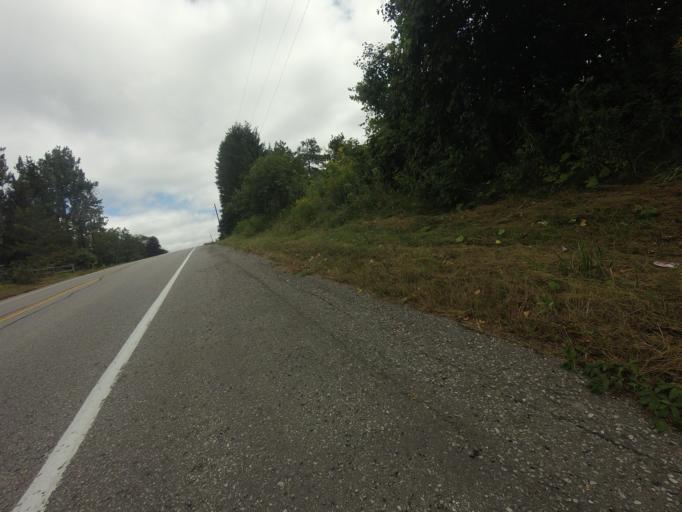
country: CA
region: Ontario
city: Uxbridge
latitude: 44.1264
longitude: -79.1621
